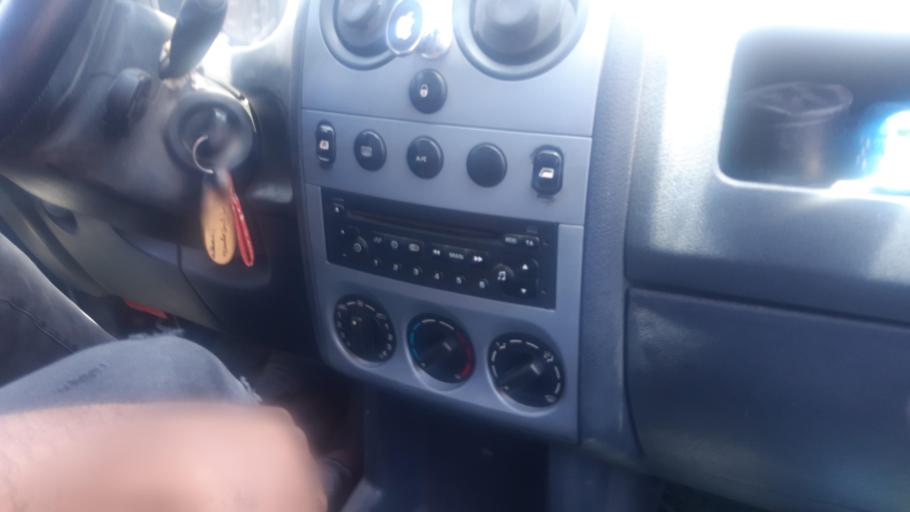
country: TN
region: Safaqis
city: Sfax
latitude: 34.6866
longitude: 10.7061
